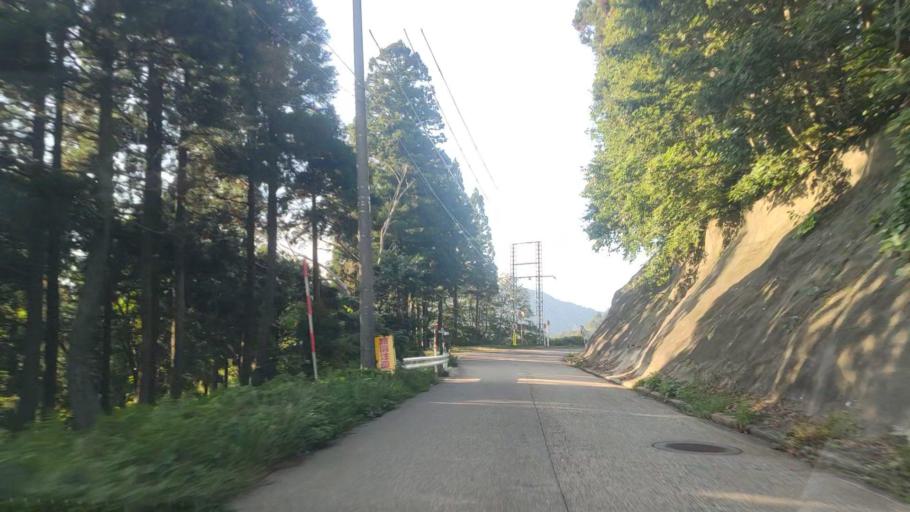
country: JP
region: Toyama
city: Yatsuomachi-higashikumisaka
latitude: 36.4931
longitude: 137.0244
